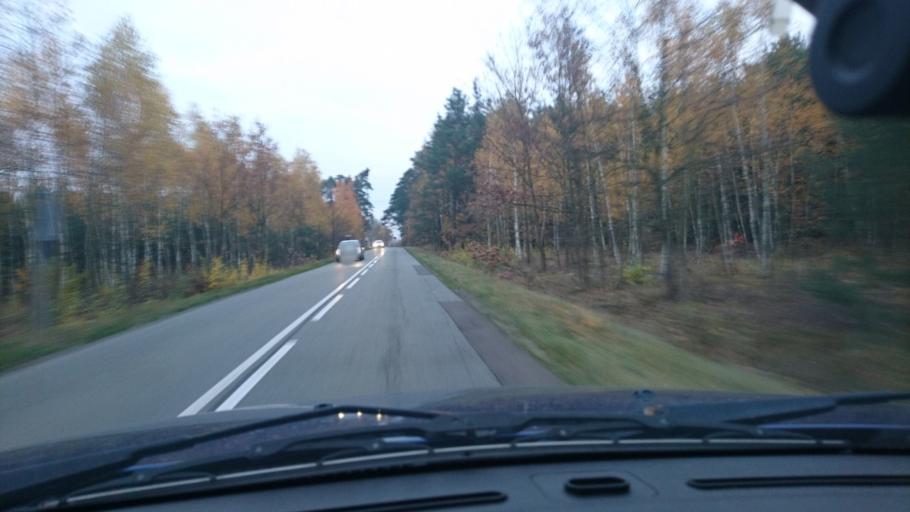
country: PL
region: Greater Poland Voivodeship
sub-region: Powiat ostrowski
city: Odolanow
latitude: 51.5292
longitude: 17.6501
